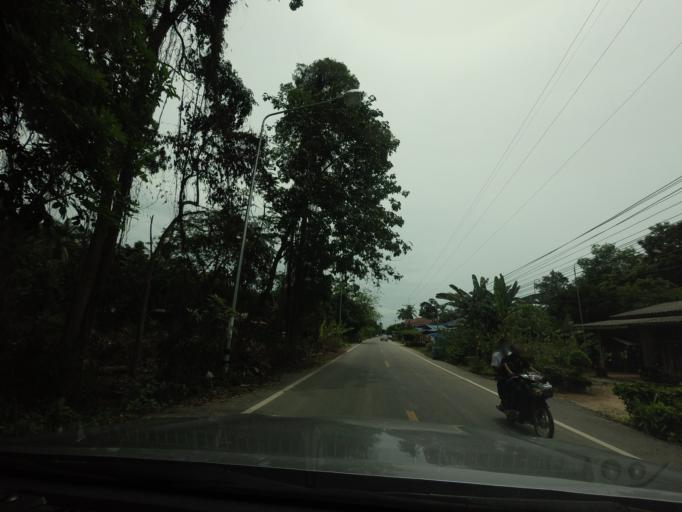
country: TH
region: Pattani
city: Kapho
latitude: 6.6158
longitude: 101.5416
